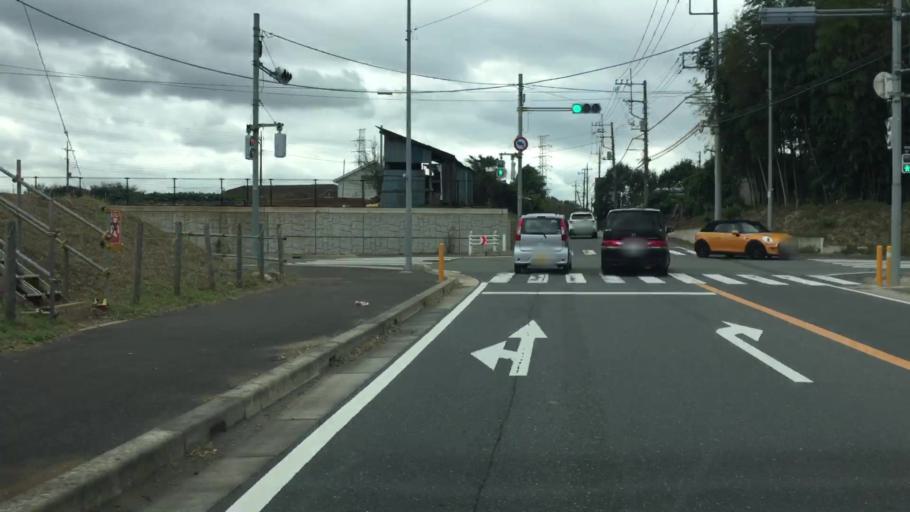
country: JP
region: Chiba
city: Shiroi
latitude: 35.8122
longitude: 140.1324
